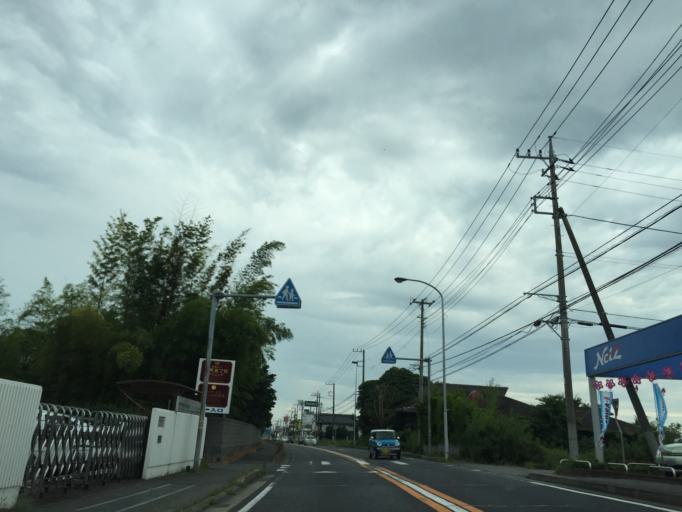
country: JP
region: Ibaraki
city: Naka
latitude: 36.0351
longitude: 140.1619
